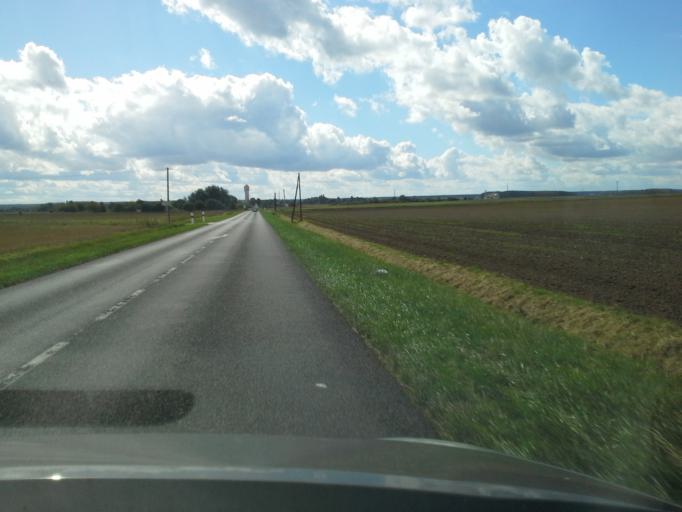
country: FR
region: Centre
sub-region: Departement du Loir-et-Cher
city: Pontlevoy
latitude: 47.4079
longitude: 1.2692
